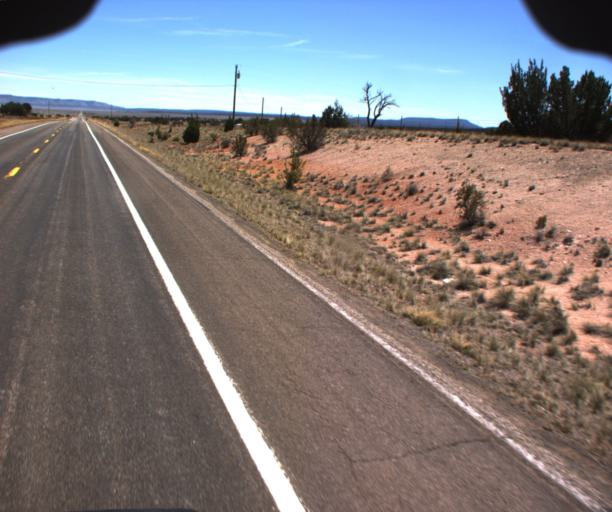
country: US
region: Arizona
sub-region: Mohave County
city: Peach Springs
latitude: 35.5014
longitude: -113.1740
